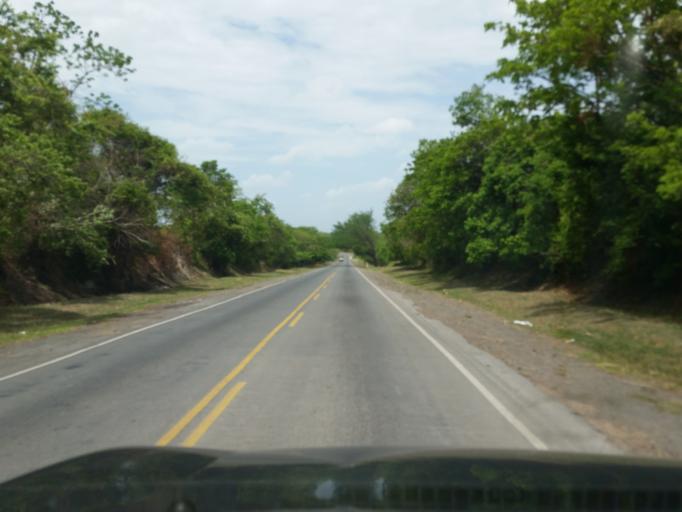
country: NI
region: Granada
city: Nandaime
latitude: 11.7980
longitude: -86.0469
